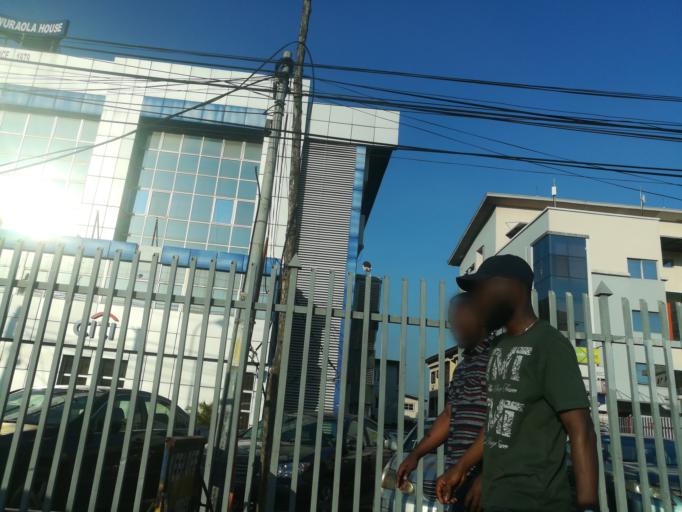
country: NG
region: Lagos
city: Ikeja
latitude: 6.6047
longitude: 3.3505
